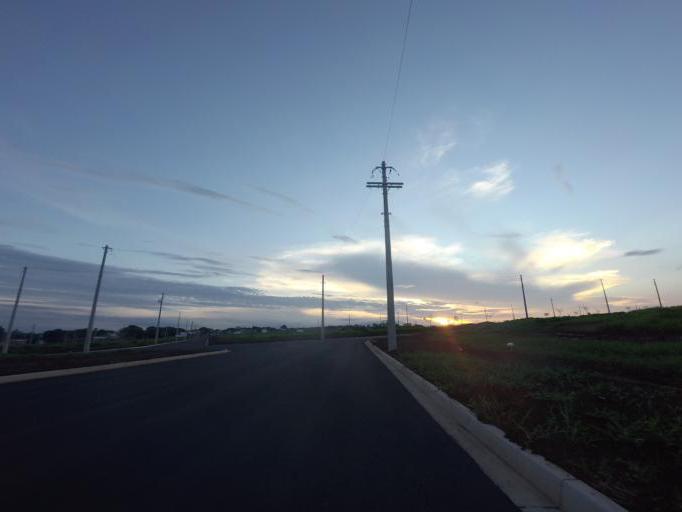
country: BR
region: Sao Paulo
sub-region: Piracicaba
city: Piracicaba
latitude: -22.7634
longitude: -47.5832
